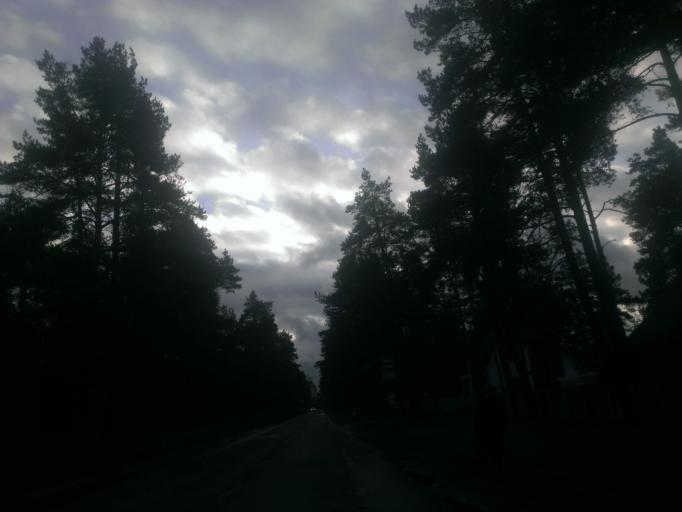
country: LV
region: Riga
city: Bolderaja
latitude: 57.0564
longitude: 24.0727
